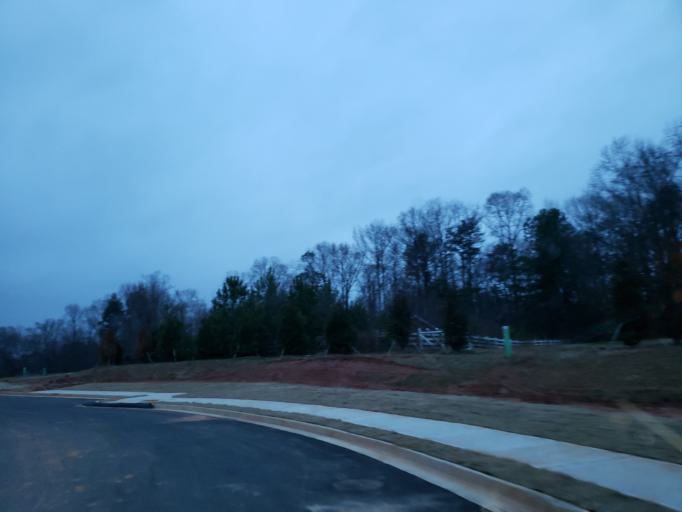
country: US
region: Georgia
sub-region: Cobb County
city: Mableton
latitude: 33.8385
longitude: -84.5833
